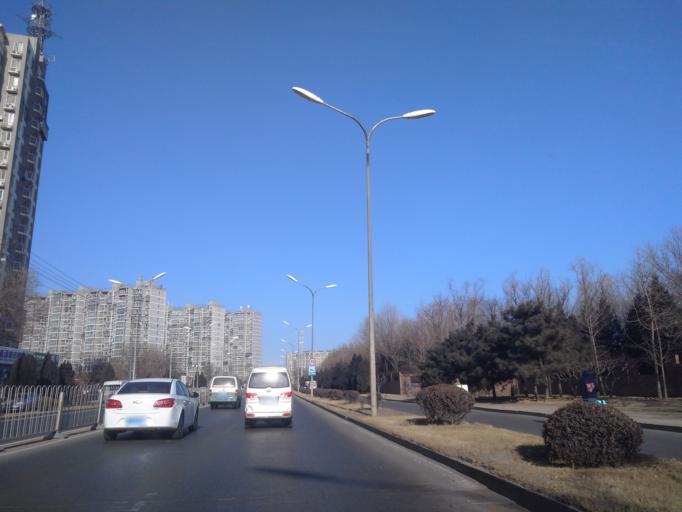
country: CN
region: Beijing
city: Jiugong
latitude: 39.8264
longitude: 116.4729
